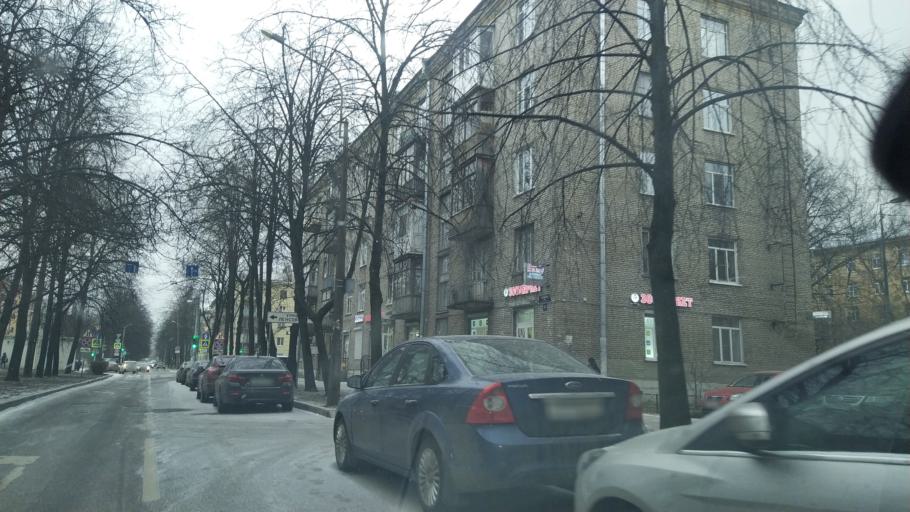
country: RU
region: St.-Petersburg
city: Kupchino
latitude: 59.8494
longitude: 30.3282
